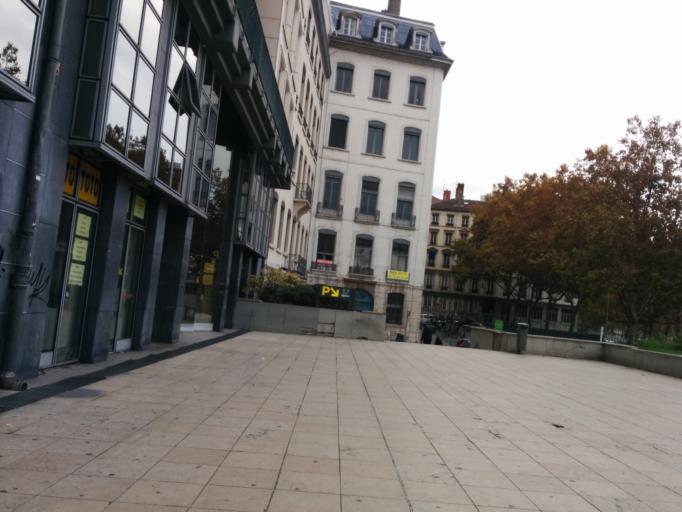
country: FR
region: Rhone-Alpes
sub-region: Departement du Rhone
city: Caluire-et-Cuire
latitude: 45.7687
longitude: 4.8374
